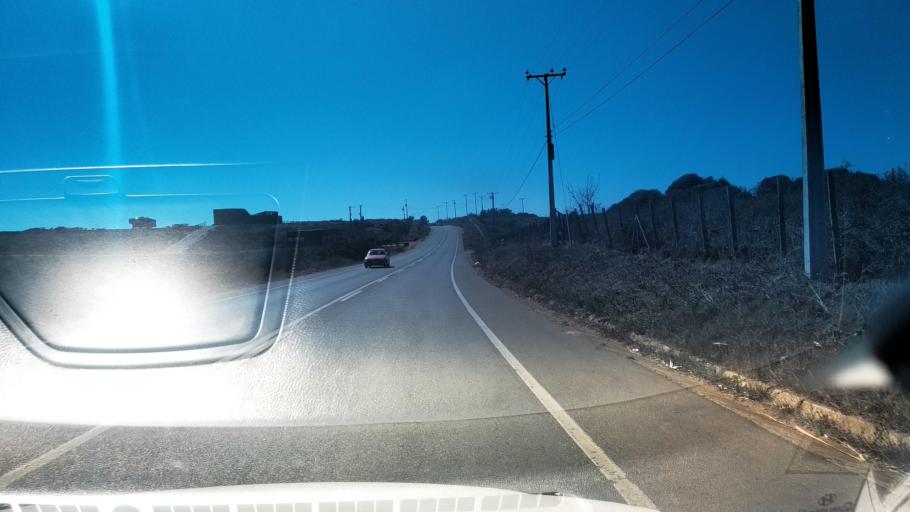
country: CL
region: O'Higgins
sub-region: Provincia de Colchagua
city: Santa Cruz
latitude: -34.4472
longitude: -72.0314
